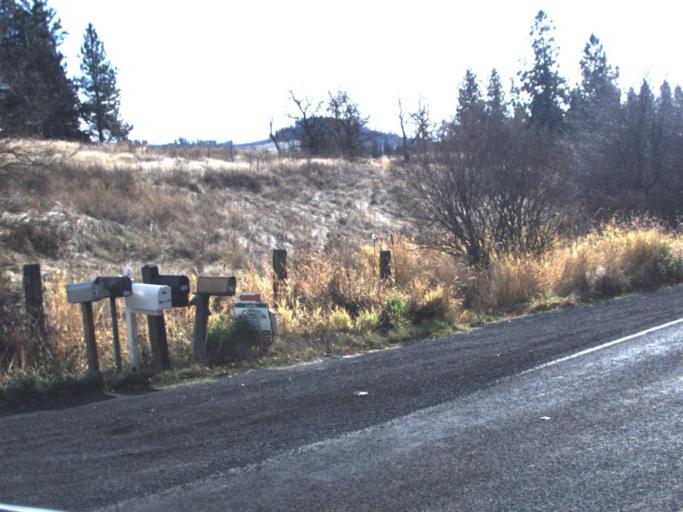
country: US
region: Idaho
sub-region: Latah County
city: Moscow
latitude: 46.9126
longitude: -117.0679
